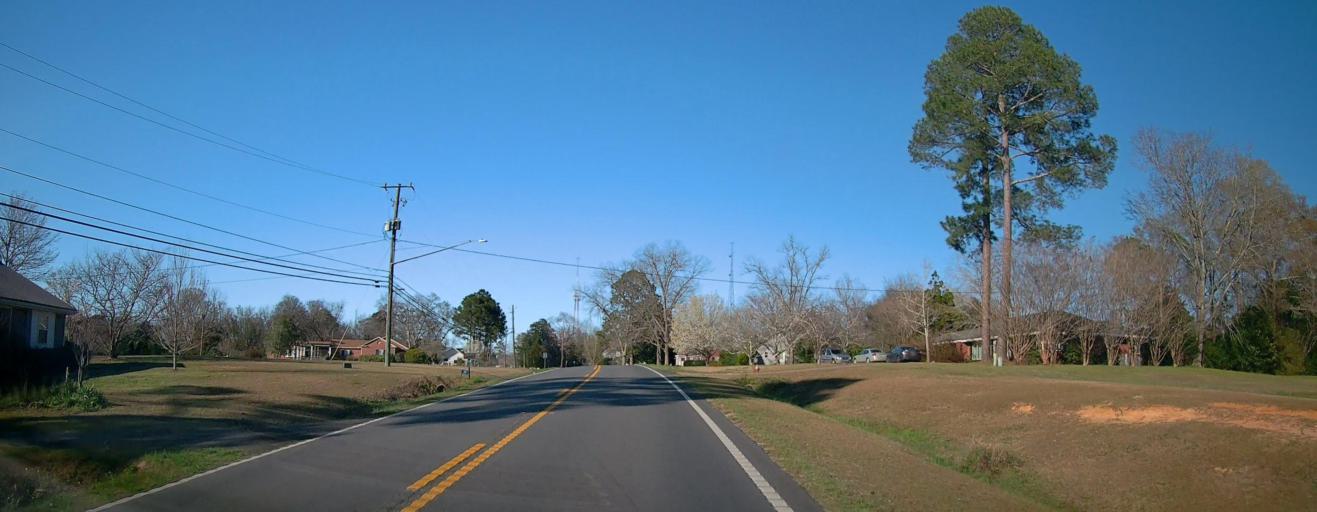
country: US
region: Georgia
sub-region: Taylor County
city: Reynolds
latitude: 32.5532
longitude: -84.0968
